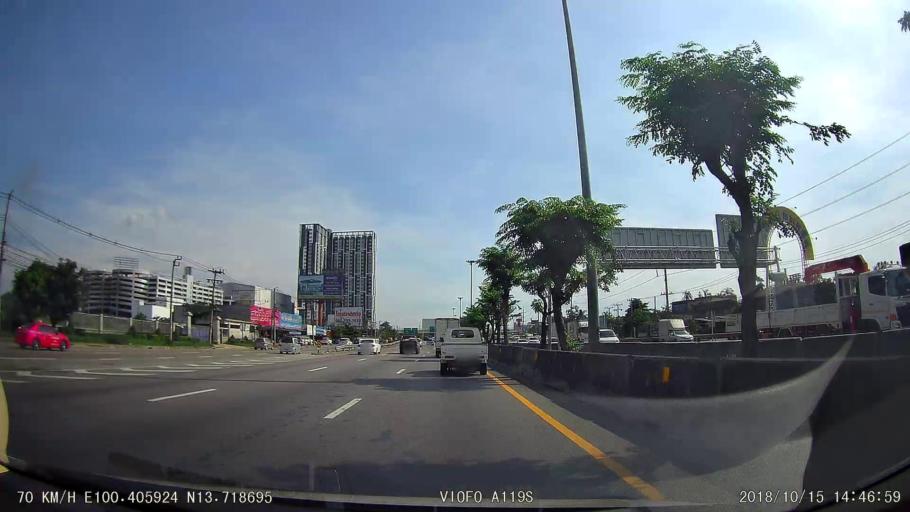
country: TH
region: Bangkok
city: Bang Khae
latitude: 13.7184
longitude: 100.4059
